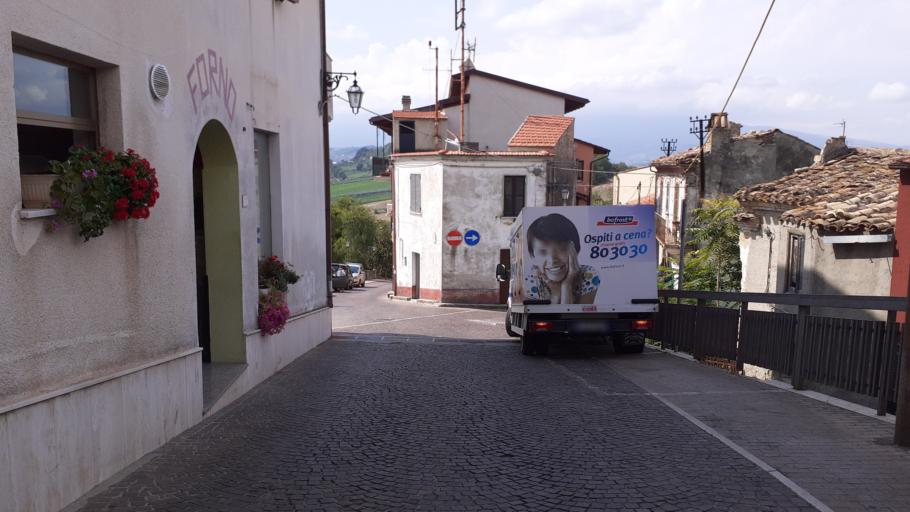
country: IT
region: Abruzzo
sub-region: Provincia di Chieti
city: Vacri
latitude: 42.2965
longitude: 14.2310
